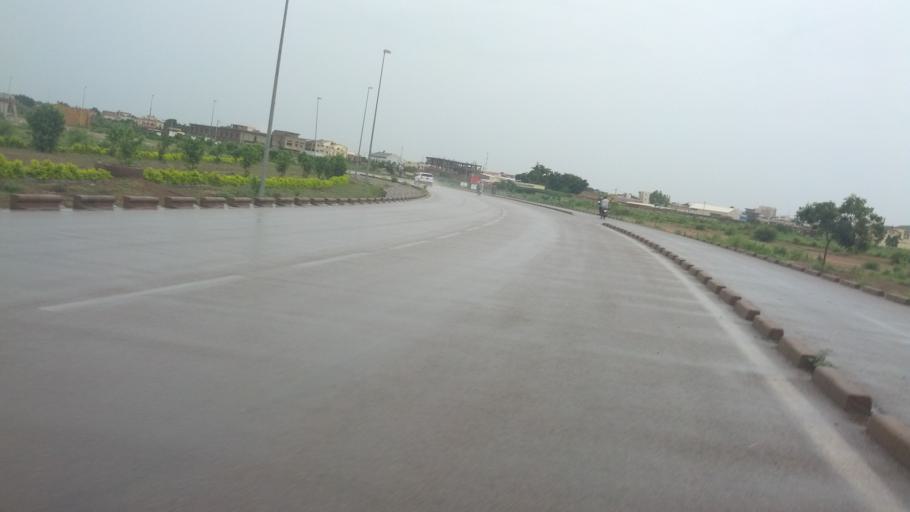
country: BF
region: Centre
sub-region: Kadiogo Province
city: Ouagadougou
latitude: 12.3145
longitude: -1.5034
